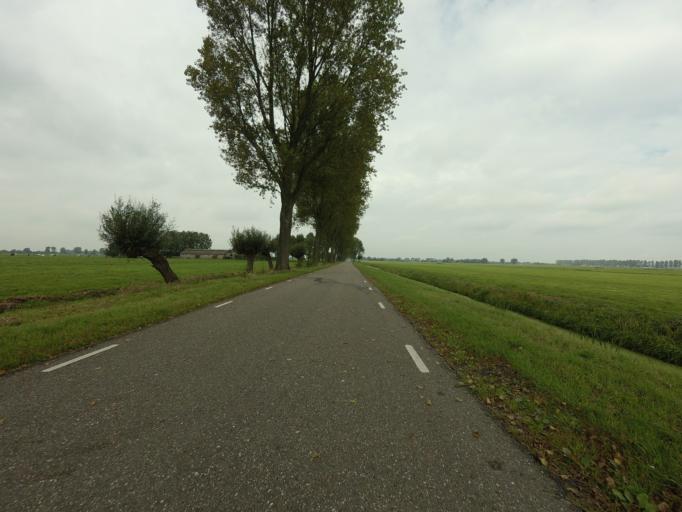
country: NL
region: Utrecht
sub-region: Gemeente Lopik
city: Lopik
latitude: 51.9091
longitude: 4.9414
